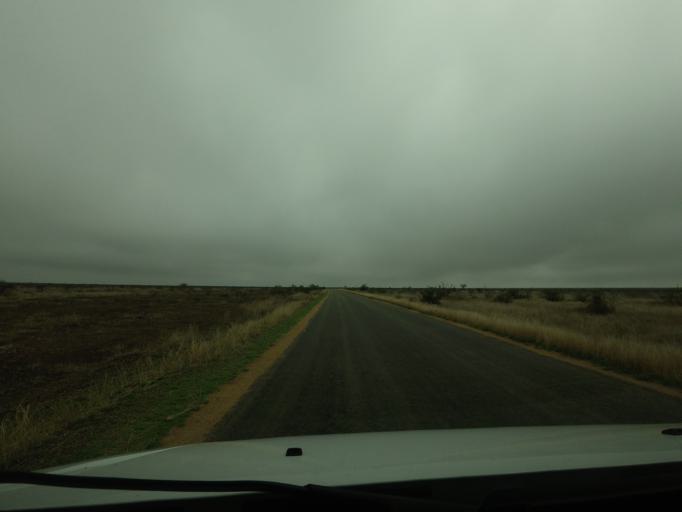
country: ZA
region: Limpopo
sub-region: Mopani District Municipality
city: Phalaborwa
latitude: -24.2424
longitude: 31.7207
